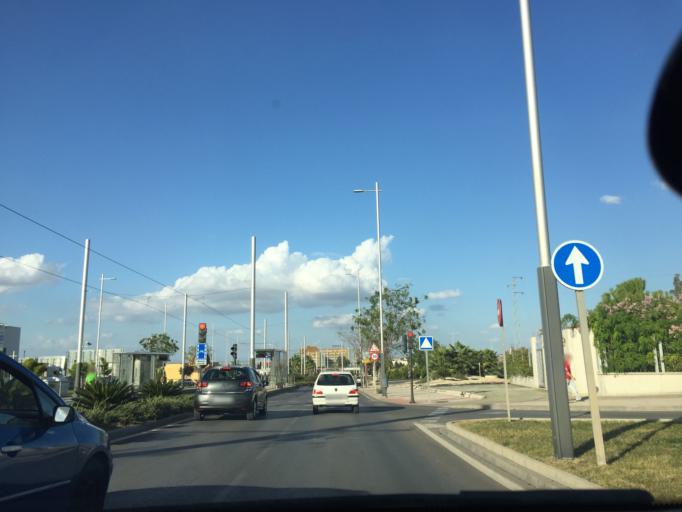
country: ES
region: Andalusia
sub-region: Provincia de Jaen
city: Jaen
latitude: 37.7893
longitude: -3.7819
